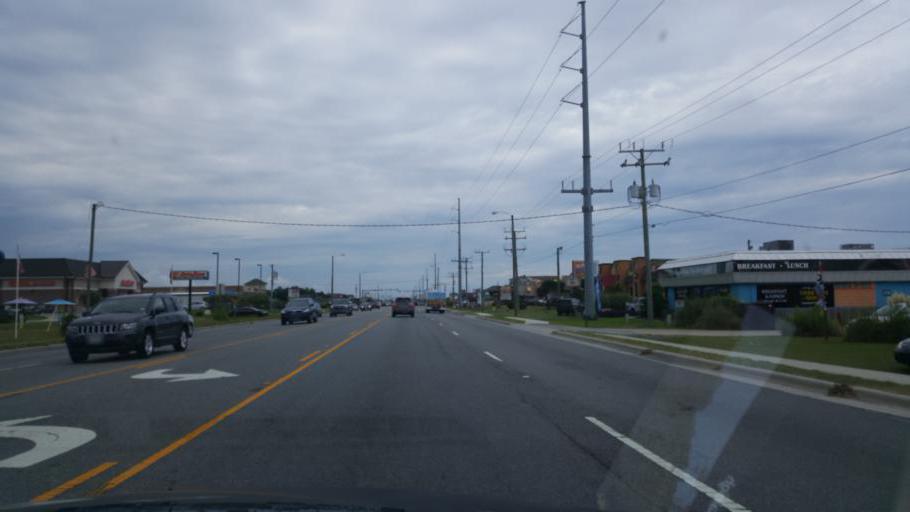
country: US
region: North Carolina
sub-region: Dare County
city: Kill Devil Hills
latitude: 36.0019
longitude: -75.6540
